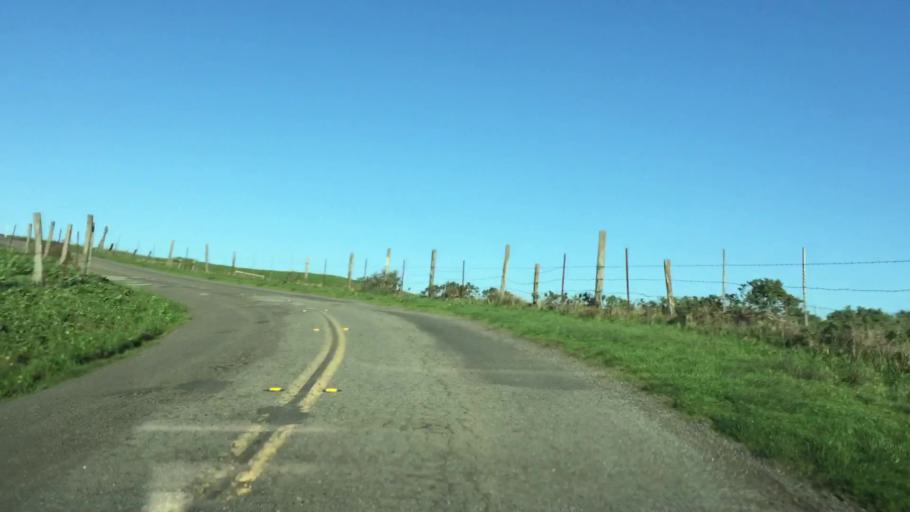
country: US
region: California
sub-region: Marin County
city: Inverness
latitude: 38.1689
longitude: -122.9347
